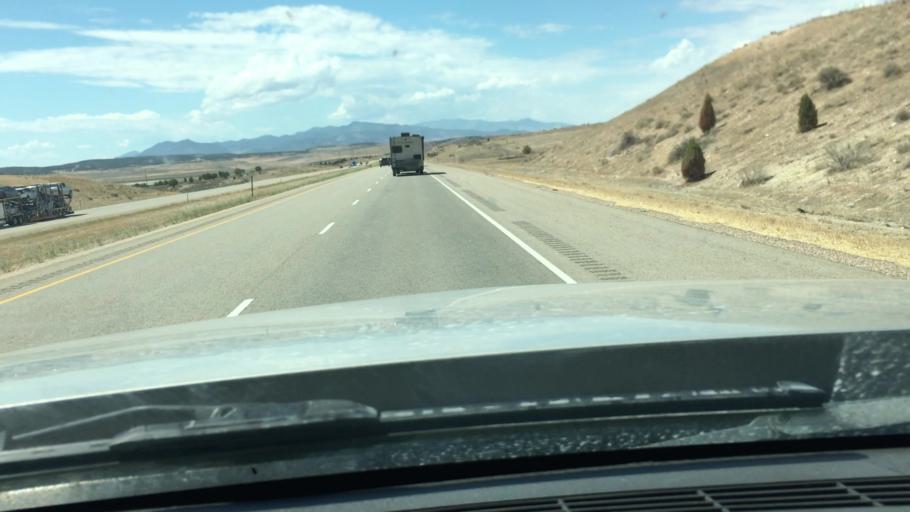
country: US
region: Utah
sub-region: Juab County
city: Nephi
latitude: 39.5175
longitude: -111.9602
